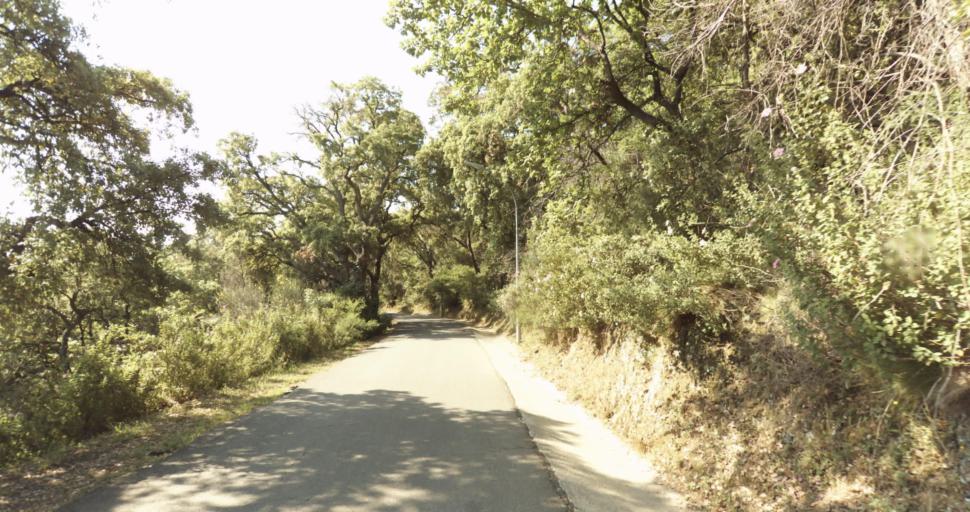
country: FR
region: Corsica
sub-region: Departement de la Haute-Corse
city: Biguglia
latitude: 42.6242
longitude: 9.4195
